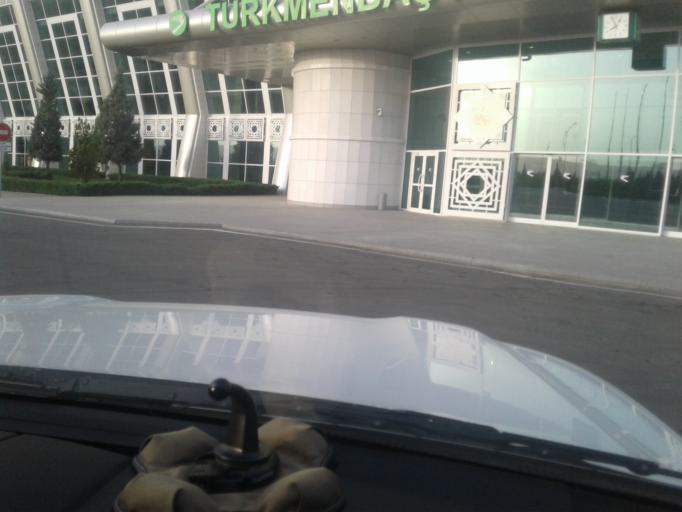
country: TM
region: Balkan
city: Turkmenbasy
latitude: 40.0437
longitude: 52.9931
